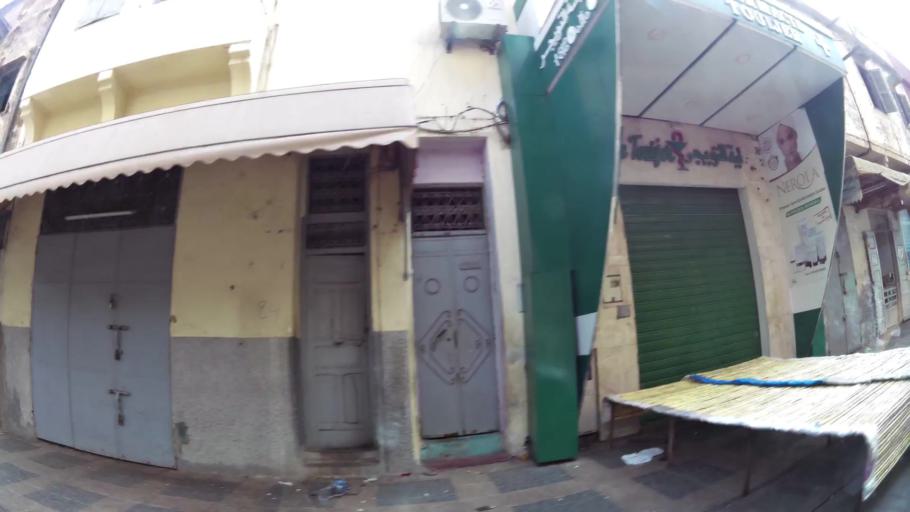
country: MA
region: Gharb-Chrarda-Beni Hssen
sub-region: Kenitra Province
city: Kenitra
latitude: 34.2630
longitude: -6.5625
